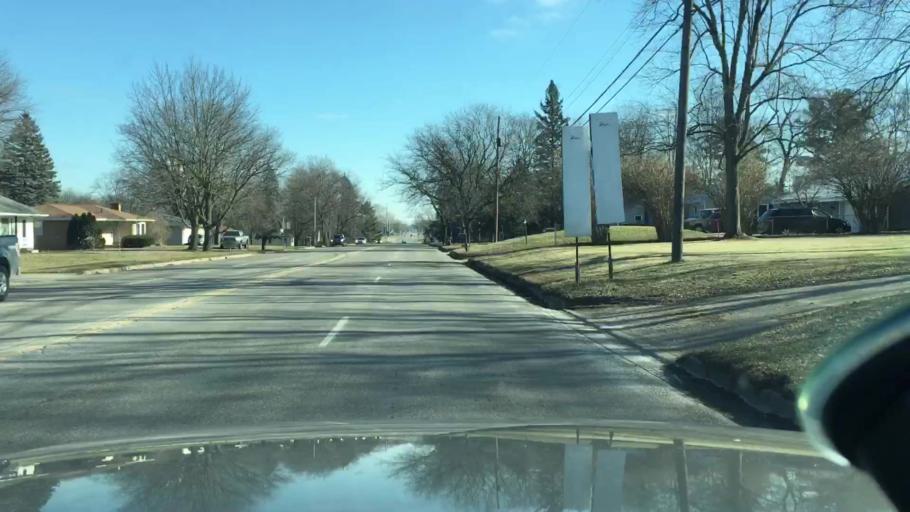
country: US
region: Michigan
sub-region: Jackson County
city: Jackson
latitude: 42.2911
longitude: -84.4299
